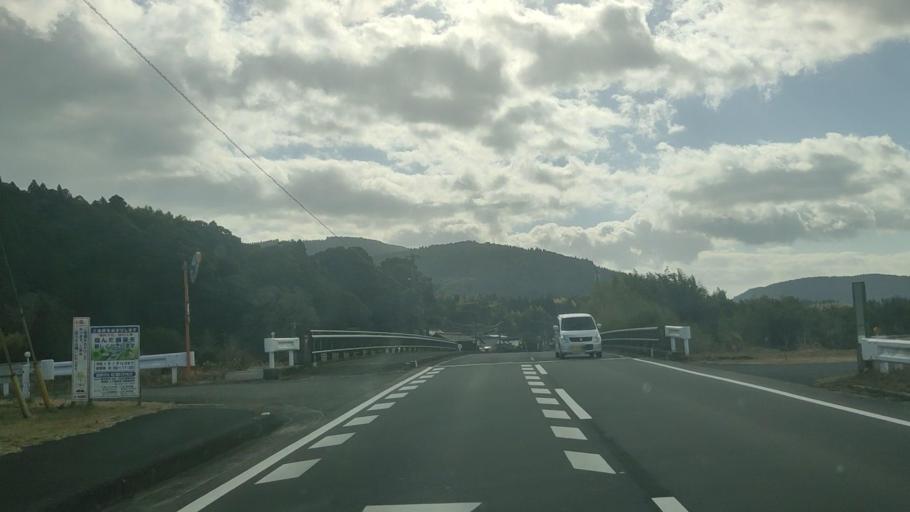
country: JP
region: Kagoshima
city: Okuchi-shinohara
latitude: 31.9944
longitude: 130.7484
